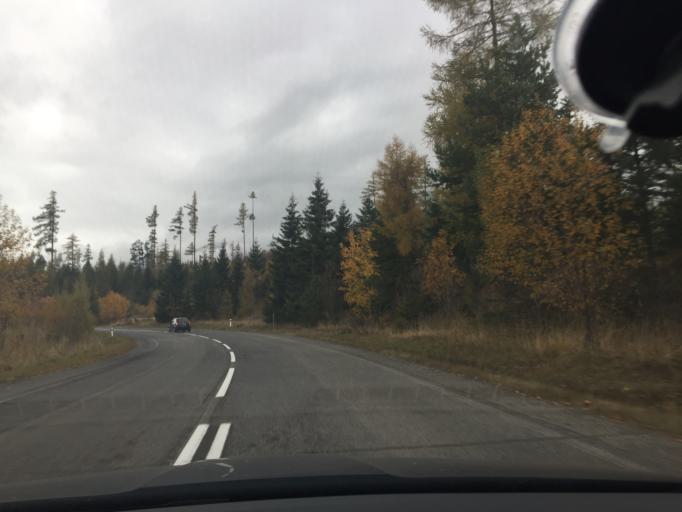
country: SK
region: Presovsky
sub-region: Okres Poprad
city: Strba
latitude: 49.1180
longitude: 20.1373
